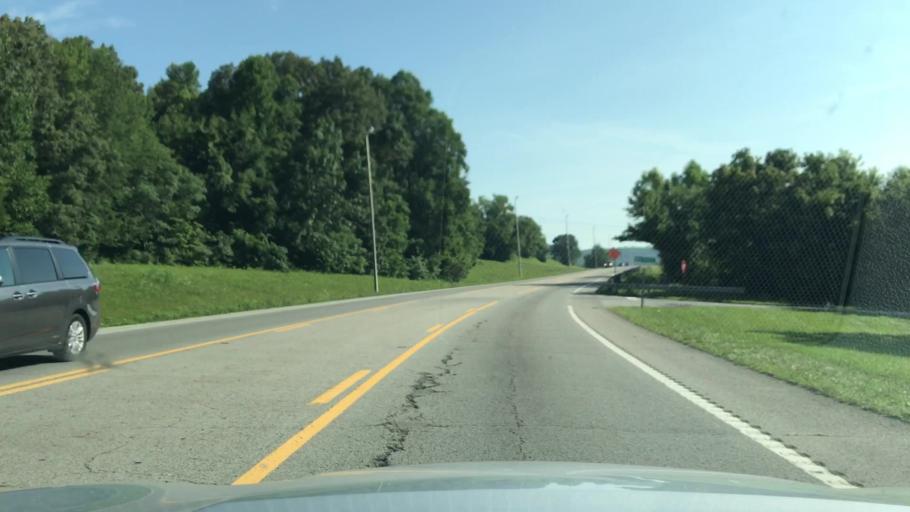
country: US
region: Tennessee
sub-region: Overton County
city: Livingston
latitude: 36.3893
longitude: -85.3345
